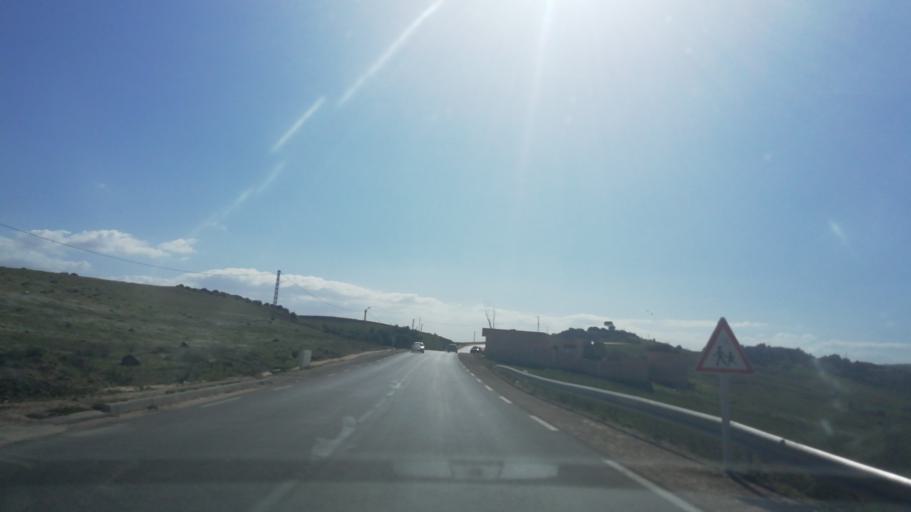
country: DZ
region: Relizane
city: Djidiouia
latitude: 36.0901
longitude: 0.5155
